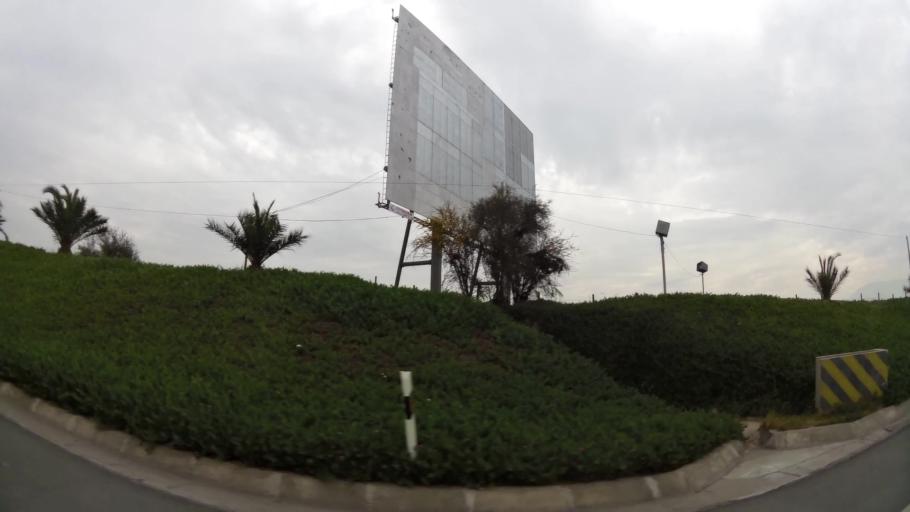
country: CL
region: Santiago Metropolitan
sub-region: Provincia de Santiago
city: Lo Prado
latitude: -33.4219
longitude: -70.7894
